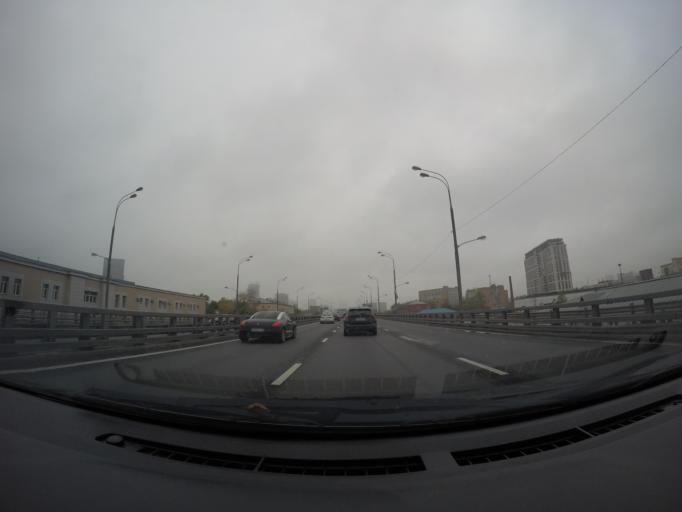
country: RU
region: Moscow
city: Sokol
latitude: 55.7682
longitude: 37.5220
